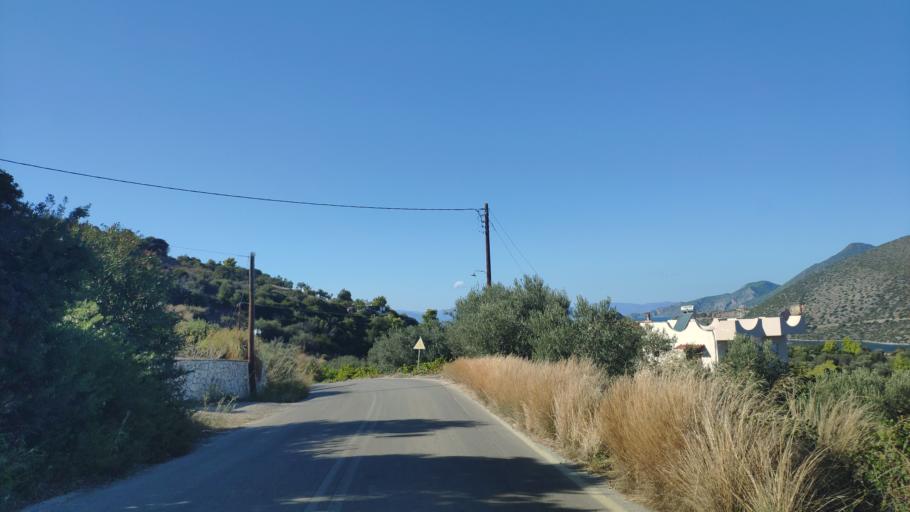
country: GR
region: Attica
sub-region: Nomos Piraios
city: Galatas
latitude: 37.5465
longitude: 23.3774
